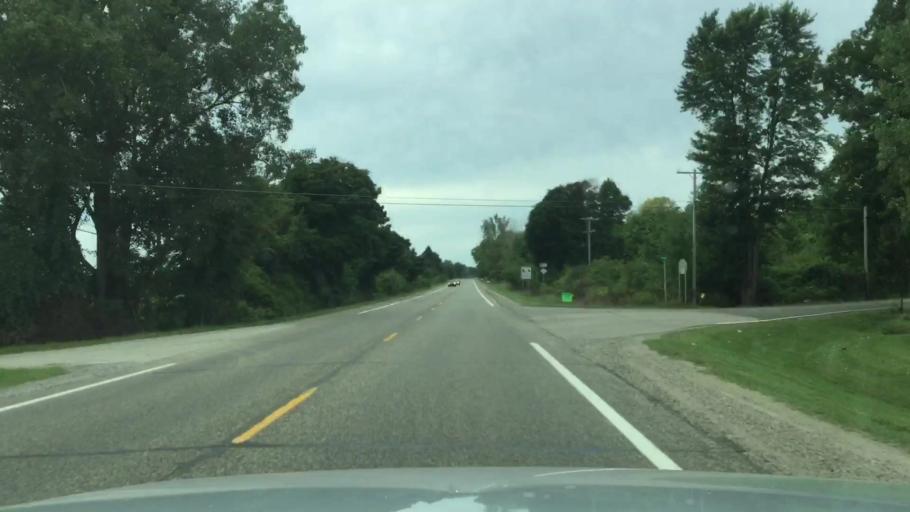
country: US
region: Michigan
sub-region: Shiawassee County
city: Durand
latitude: 42.9321
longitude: -84.0079
